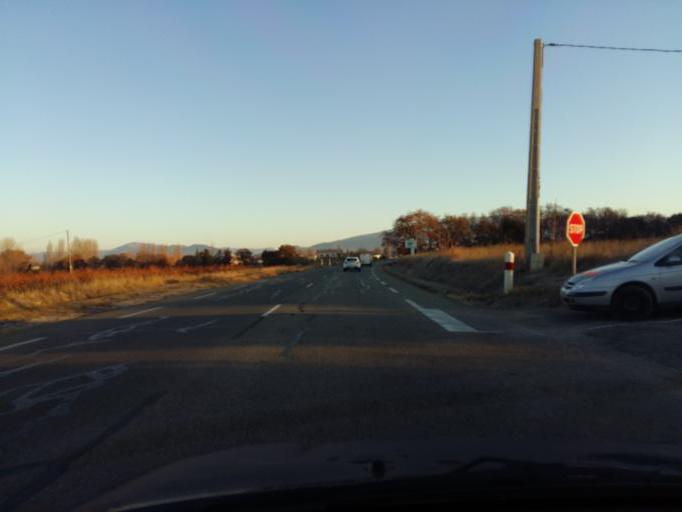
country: FR
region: Provence-Alpes-Cote d'Azur
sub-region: Departement du Vaucluse
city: Valreas
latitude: 44.3636
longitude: 4.9743
